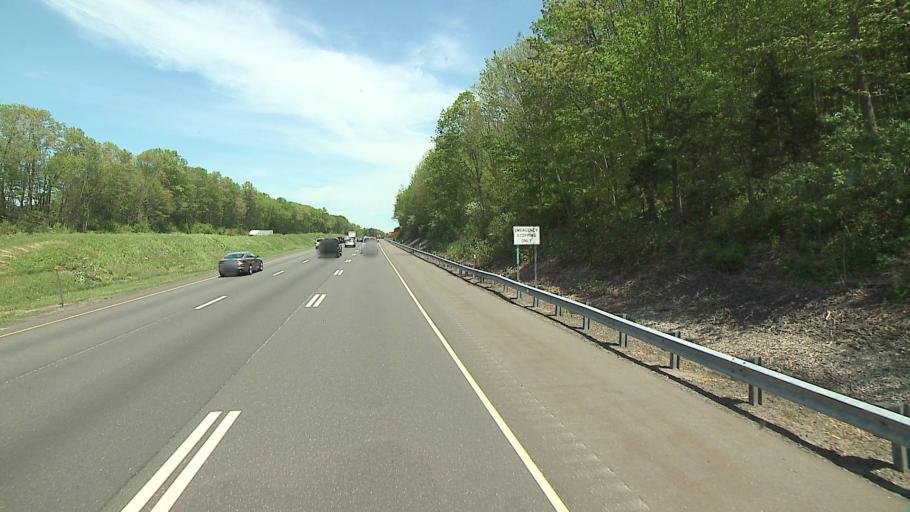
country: US
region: Connecticut
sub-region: New Haven County
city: Middlebury
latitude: 41.4978
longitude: -73.1565
